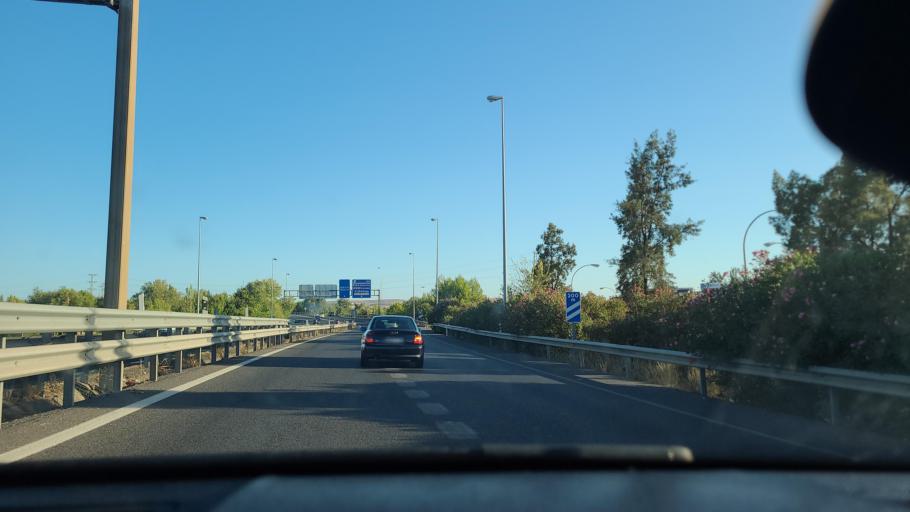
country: ES
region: Andalusia
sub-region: Province of Cordoba
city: Cordoba
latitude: 37.8927
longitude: -4.7456
